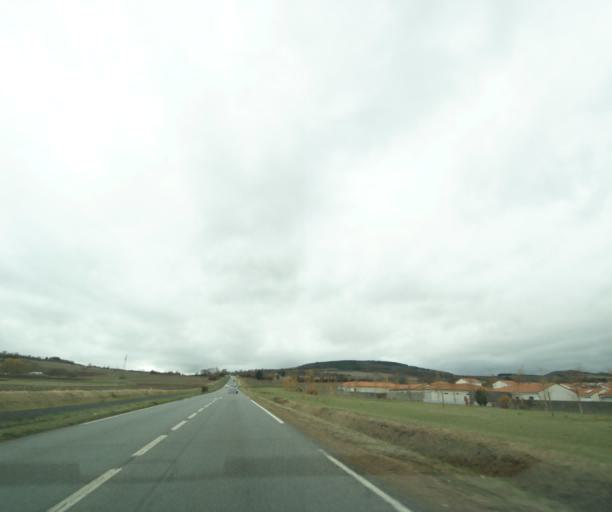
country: FR
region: Auvergne
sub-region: Departement du Puy-de-Dome
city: Dallet
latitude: 45.7694
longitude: 3.2078
